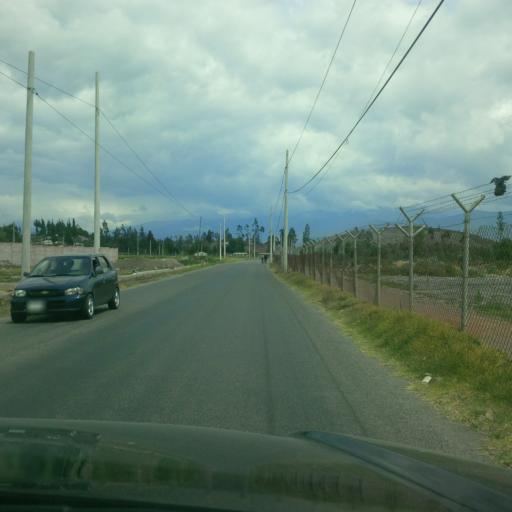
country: EC
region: Chimborazo
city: Riobamba
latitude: -1.6424
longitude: -78.6553
